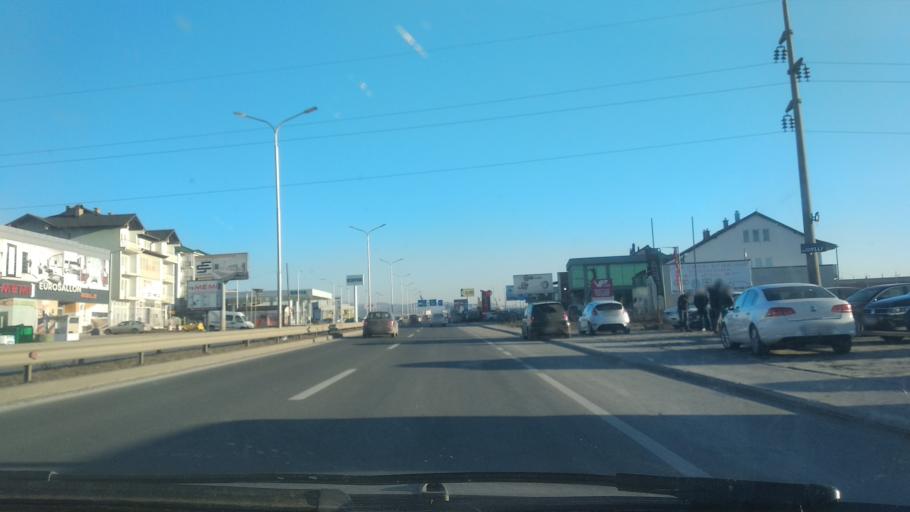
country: XK
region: Pristina
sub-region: Komuna e Prishtines
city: Pristina
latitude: 42.6602
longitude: 21.1329
